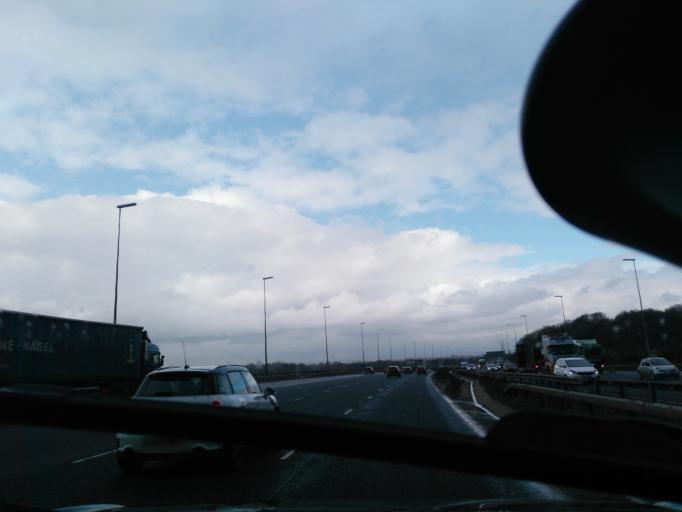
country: GB
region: England
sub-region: Warrington
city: Lymm
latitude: 53.3654
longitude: -2.5100
